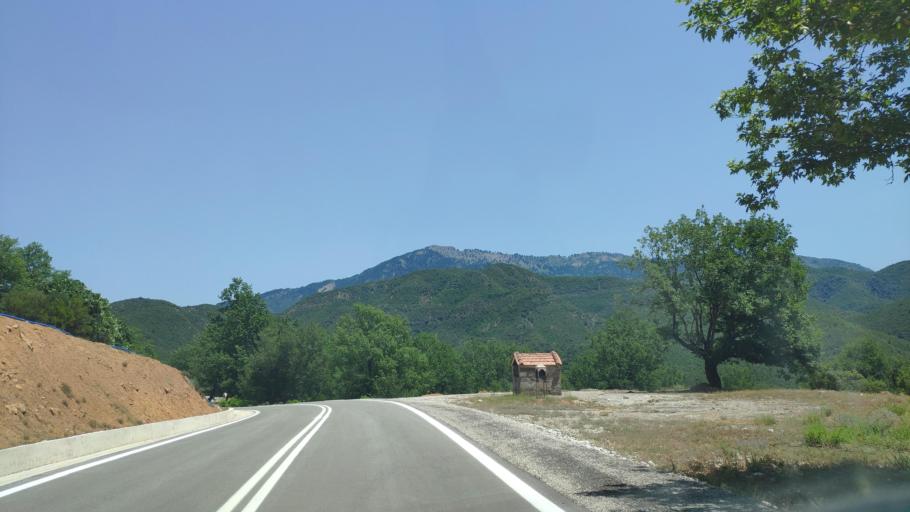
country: GR
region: Epirus
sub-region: Nomos Artas
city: Ano Kalentini
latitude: 39.1819
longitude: 21.3567
